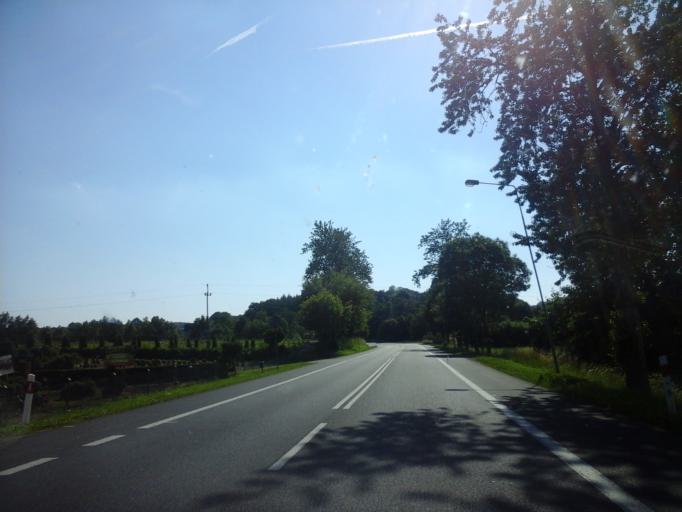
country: PL
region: West Pomeranian Voivodeship
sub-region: Powiat kolobrzeski
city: Ryman
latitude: 53.9612
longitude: 15.5742
